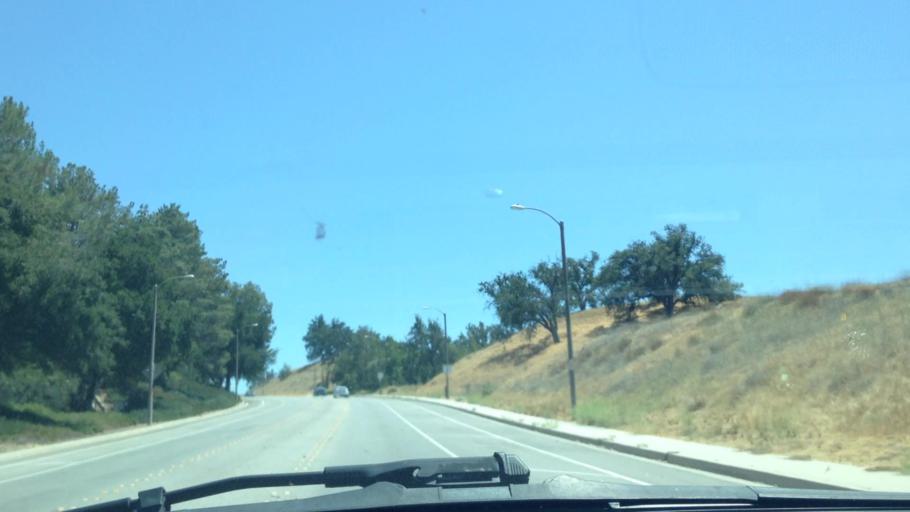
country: US
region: California
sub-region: Los Angeles County
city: Santa Clarita
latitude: 34.3995
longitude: -118.5668
